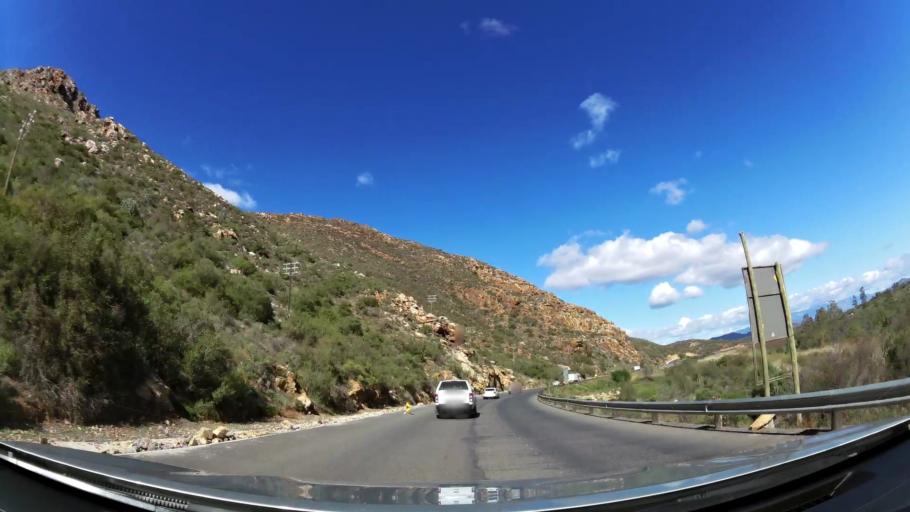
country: ZA
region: Western Cape
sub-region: Cape Winelands District Municipality
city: Ashton
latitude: -33.8206
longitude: 20.0917
